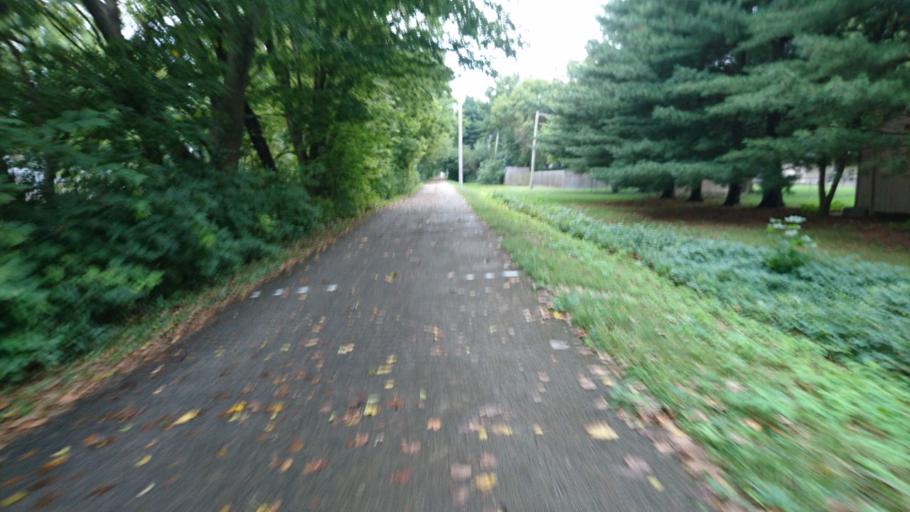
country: US
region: Illinois
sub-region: Sangamon County
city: Chatham
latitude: 39.6833
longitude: -89.6993
